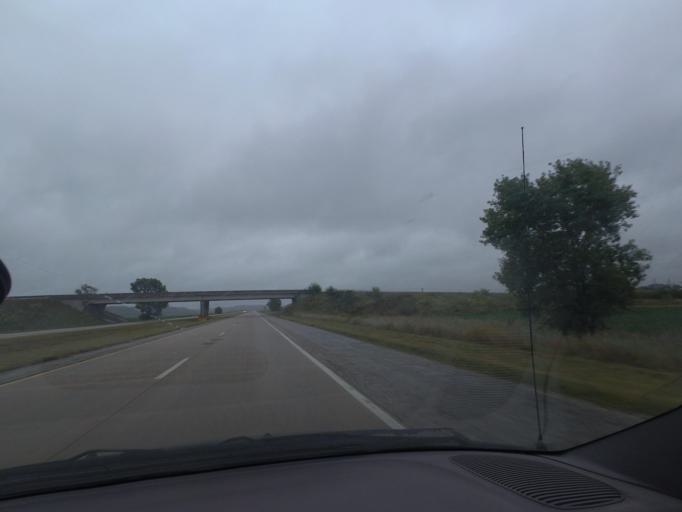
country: US
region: Illinois
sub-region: Adams County
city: Payson
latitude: 39.7210
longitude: -91.2149
